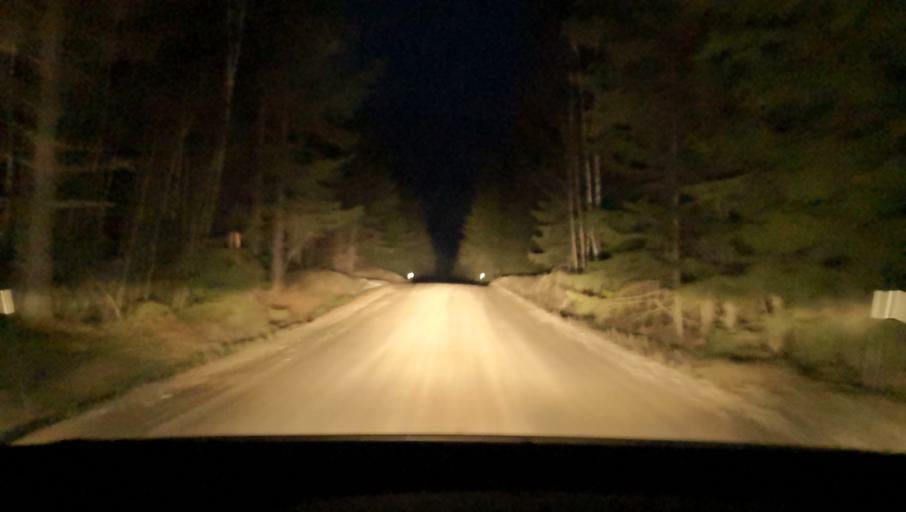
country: SE
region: Vaestmanland
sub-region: Skinnskattebergs Kommun
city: Skinnskatteberg
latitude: 59.6641
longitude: 15.5744
